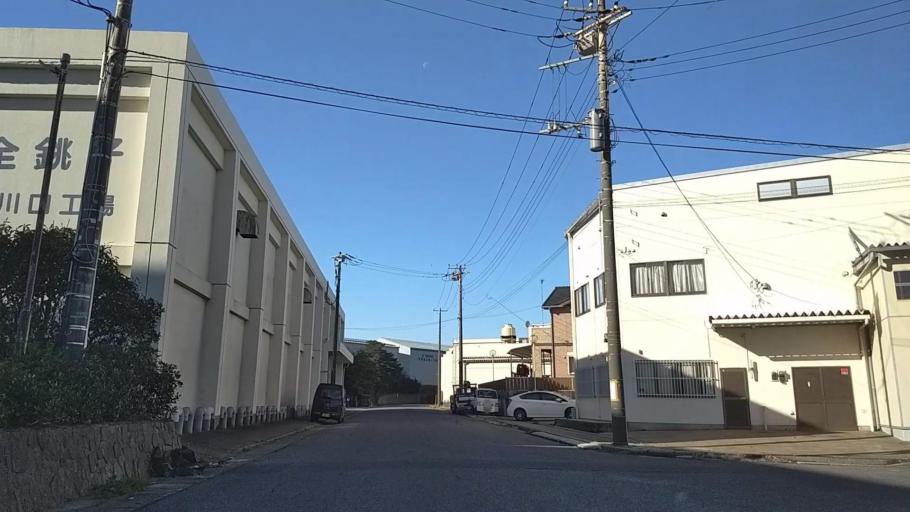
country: JP
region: Chiba
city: Hasaki
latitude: 35.7413
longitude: 140.8624
